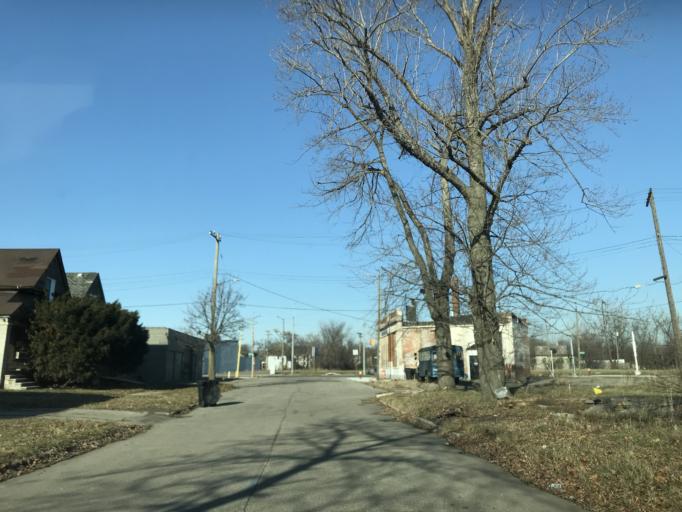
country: US
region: Michigan
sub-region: Wayne County
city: Dearborn
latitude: 42.3438
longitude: -83.1172
